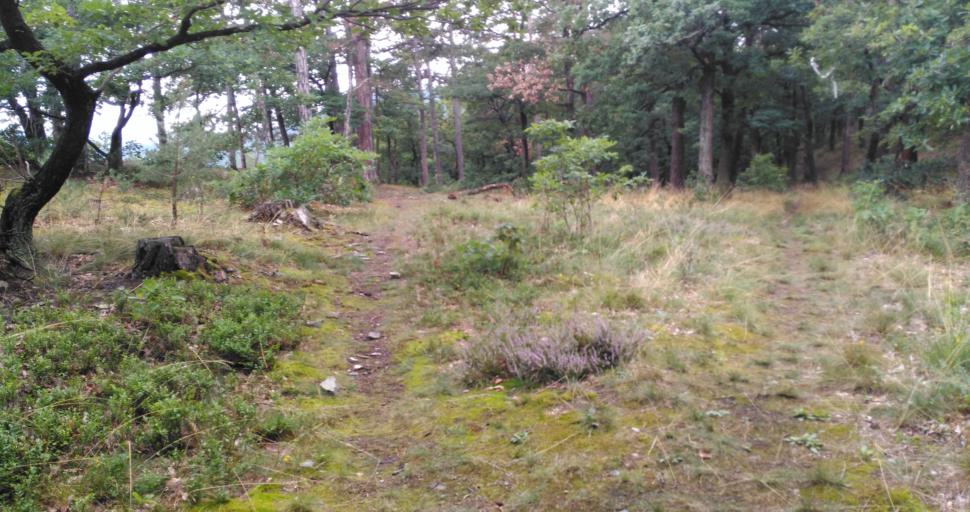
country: CZ
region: Central Bohemia
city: Jince
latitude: 49.7761
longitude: 13.9631
